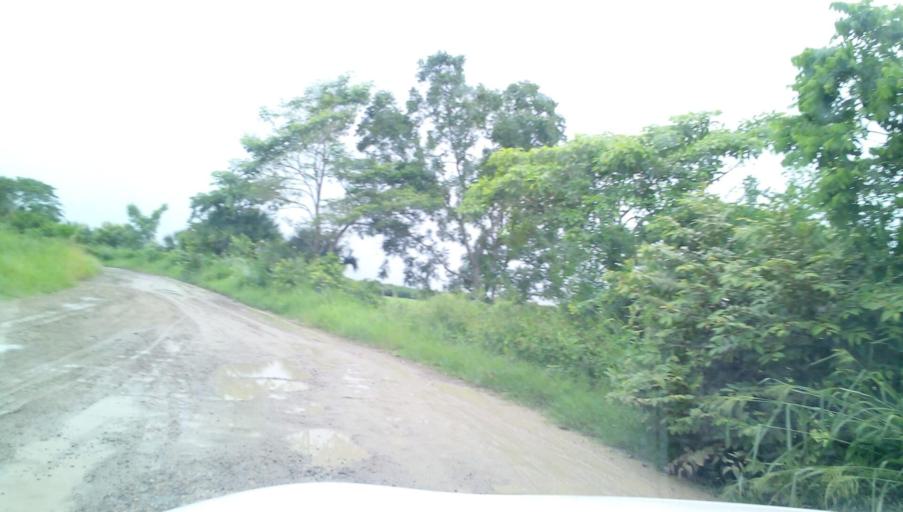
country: MX
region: Veracruz
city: Panuco
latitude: 21.8084
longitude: -98.1060
